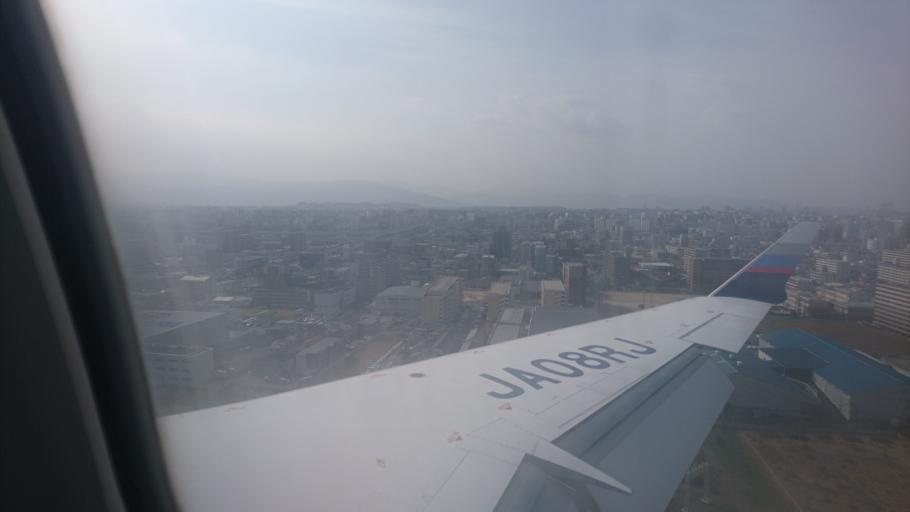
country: JP
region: Fukuoka
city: Fukuoka-shi
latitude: 33.6056
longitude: 130.4371
